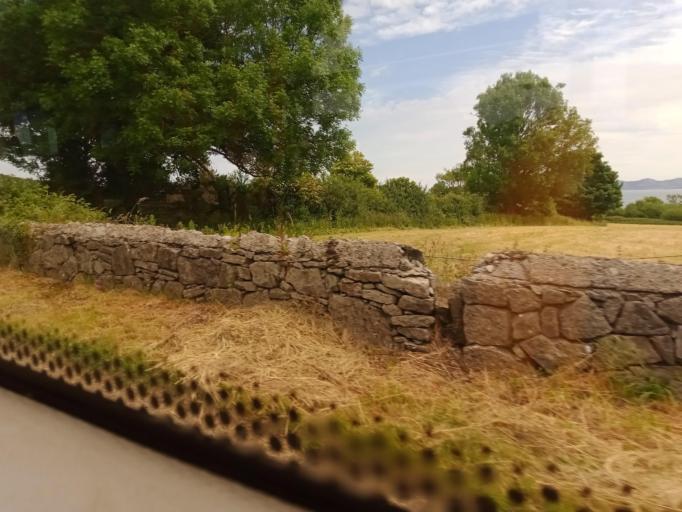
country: GB
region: Wales
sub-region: Anglesey
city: Llangoed
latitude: 53.2949
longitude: -4.0702
